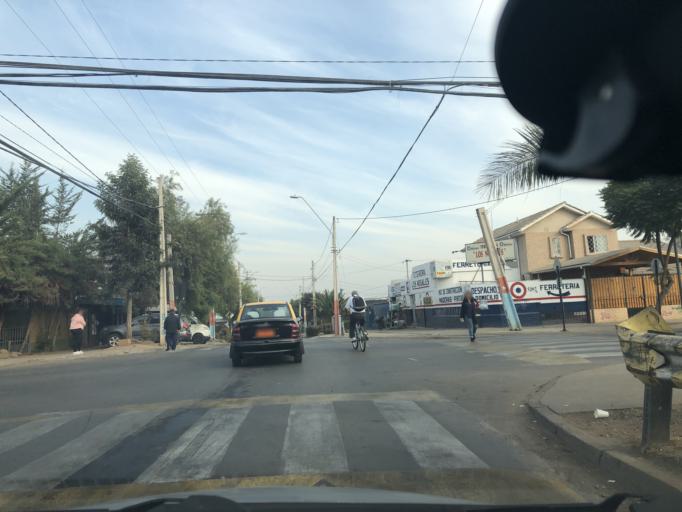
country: CL
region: Santiago Metropolitan
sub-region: Provincia de Cordillera
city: Puente Alto
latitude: -33.5845
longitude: -70.5572
